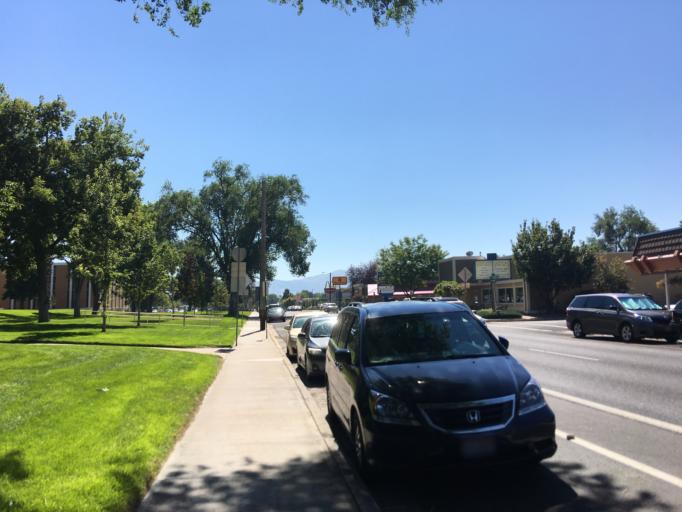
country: US
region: Idaho
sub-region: Bannock County
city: Pocatello
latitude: 42.8608
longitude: -112.4368
